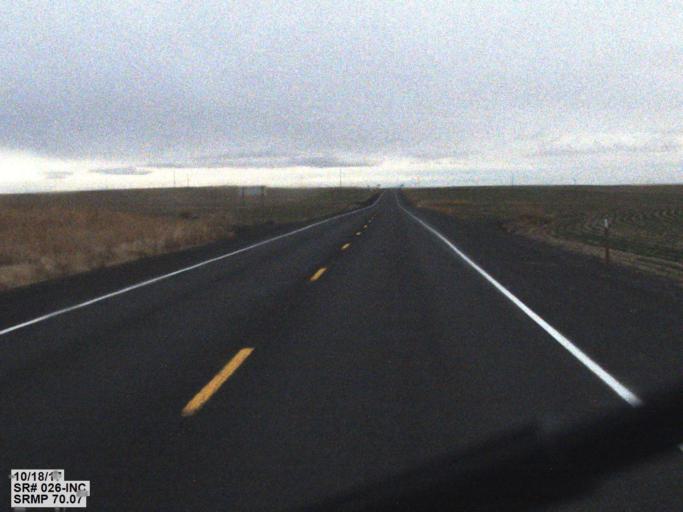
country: US
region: Washington
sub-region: Franklin County
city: Connell
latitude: 46.7948
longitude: -118.5583
